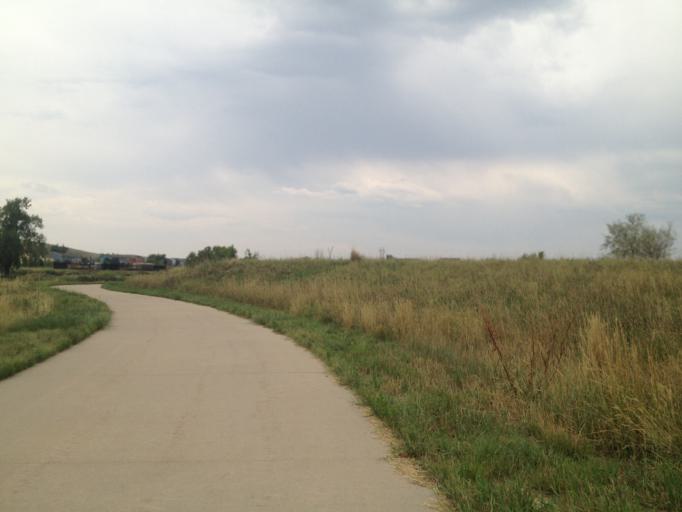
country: US
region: Colorado
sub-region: Boulder County
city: Erie
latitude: 40.0425
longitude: -105.0443
